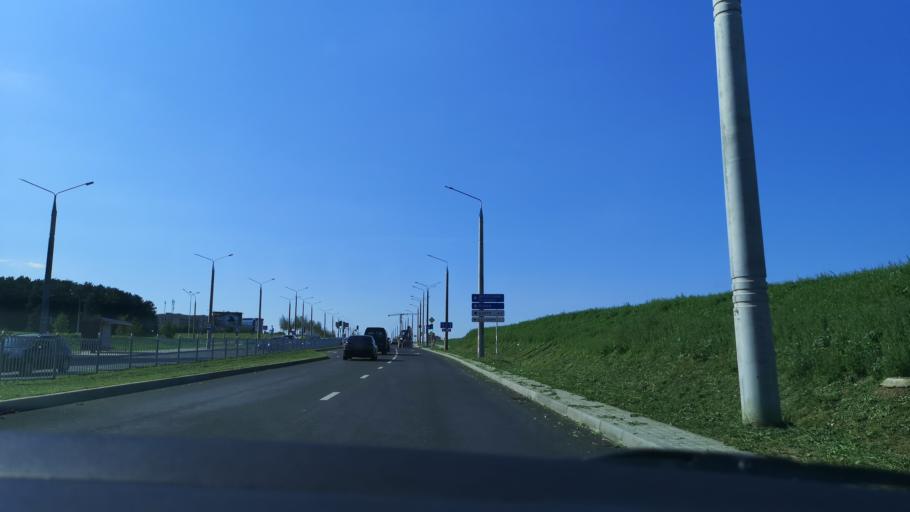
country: BY
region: Grodnenskaya
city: Hrodna
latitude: 53.6466
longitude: 23.8682
